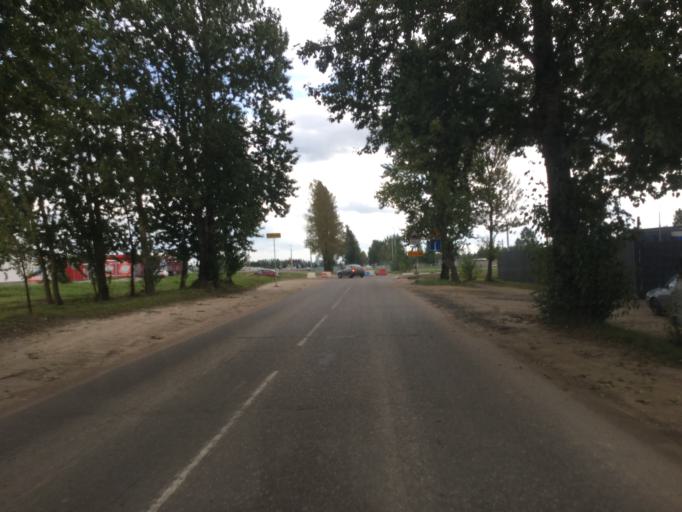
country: BY
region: Vitebsk
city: Vitebsk
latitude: 55.1680
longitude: 30.2519
